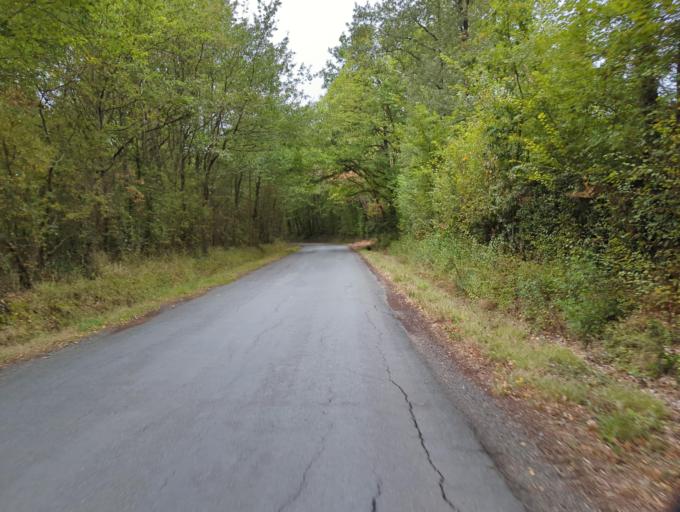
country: FR
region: Pays de la Loire
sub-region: Departement de Maine-et-Loire
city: Trelaze
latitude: 47.4731
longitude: -0.4532
